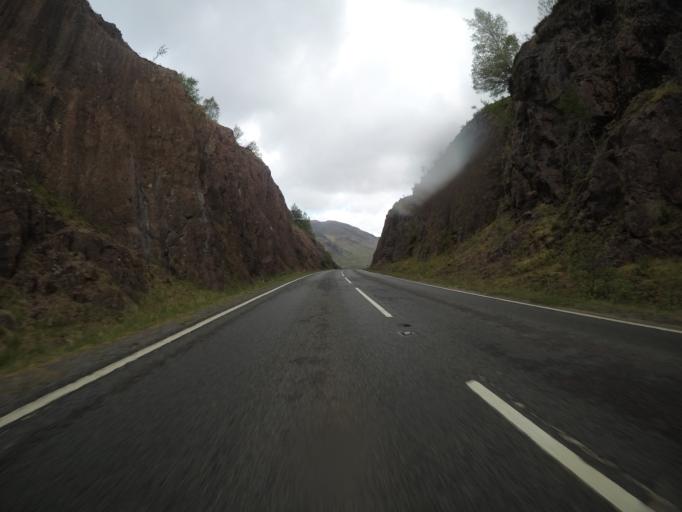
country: GB
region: Scotland
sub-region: Highland
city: Fort William
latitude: 57.2221
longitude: -5.4155
